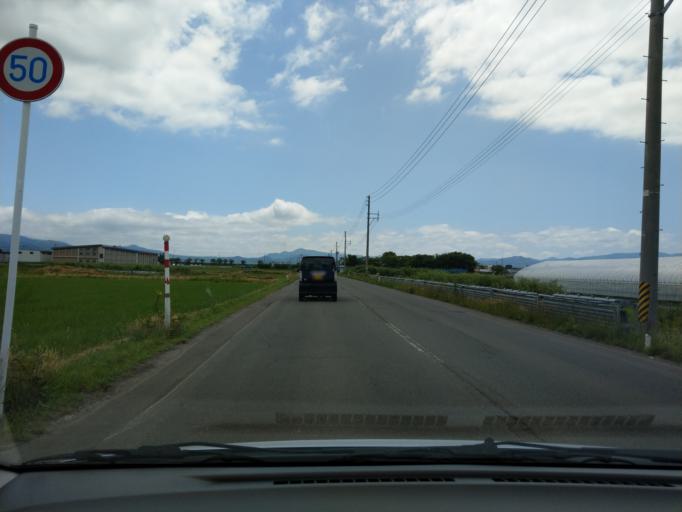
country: JP
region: Aomori
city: Kuroishi
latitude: 40.6406
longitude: 140.5669
